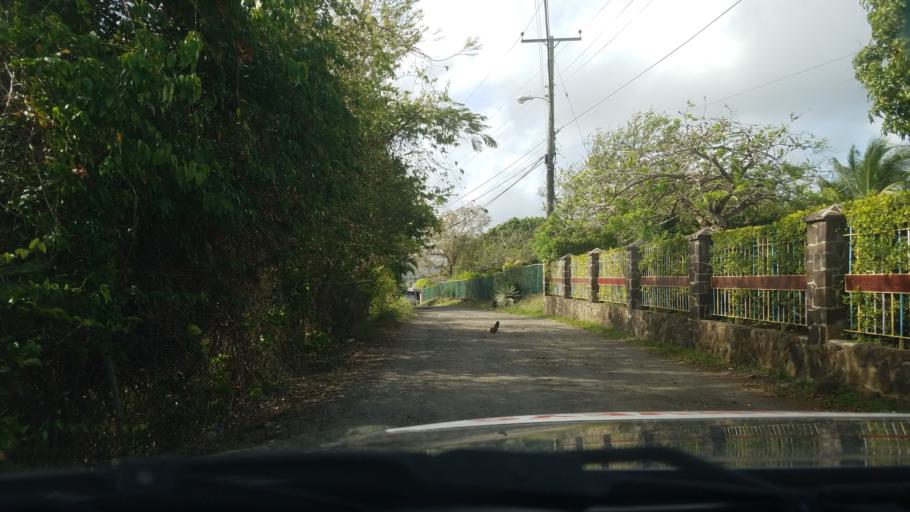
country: LC
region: Gros-Islet
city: Gros Islet
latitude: 14.0511
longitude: -60.9702
